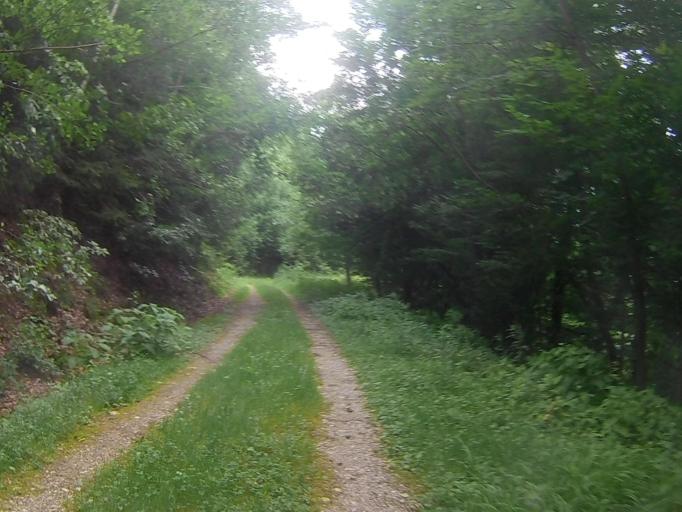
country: SI
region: Selnica ob Dravi
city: Selnica ob Dravi
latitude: 46.5211
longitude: 15.4862
